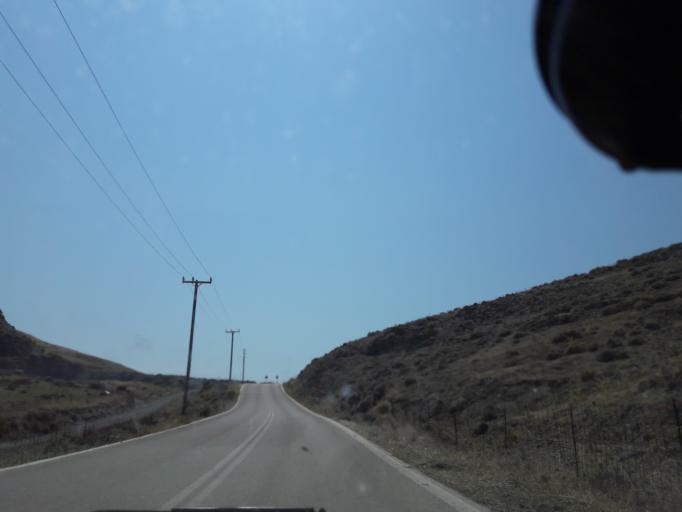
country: GR
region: North Aegean
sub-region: Nomos Lesvou
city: Myrina
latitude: 39.8513
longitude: 25.0950
